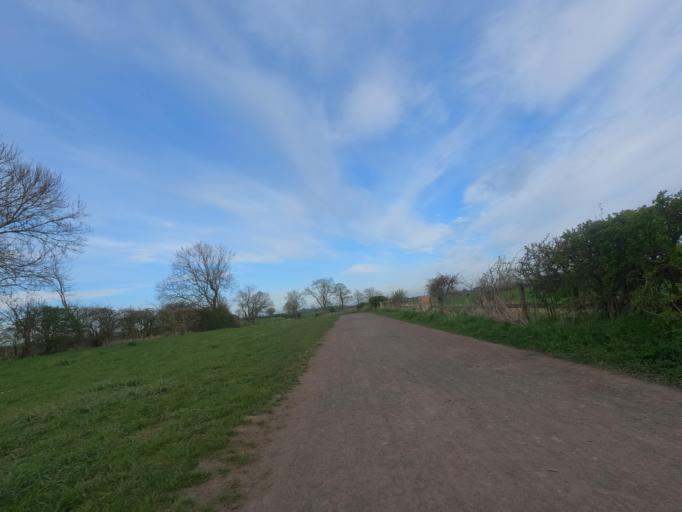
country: GB
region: England
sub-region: Newcastle upon Tyne
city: Dinnington
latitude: 55.0582
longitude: -1.6586
